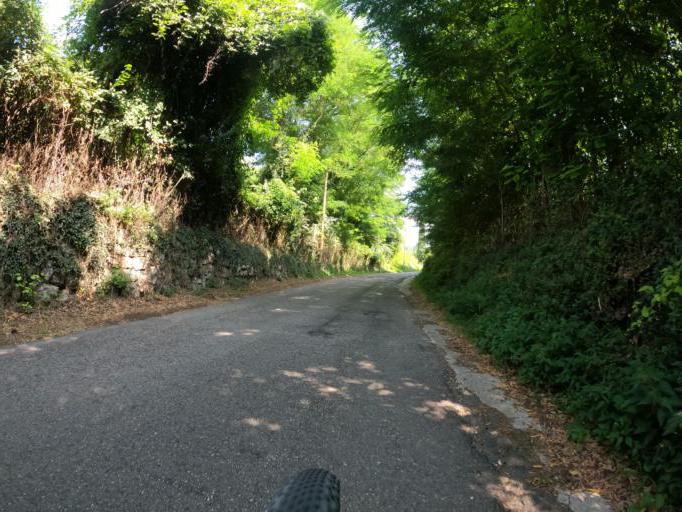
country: IT
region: Veneto
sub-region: Provincia di Verona
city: Caprino Veronese
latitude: 45.6148
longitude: 10.8075
